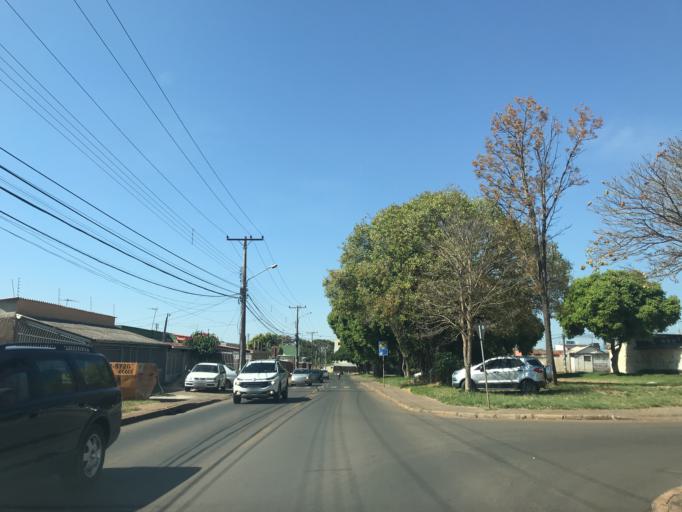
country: BR
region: Federal District
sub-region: Brasilia
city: Brasilia
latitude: -15.8158
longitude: -48.0807
